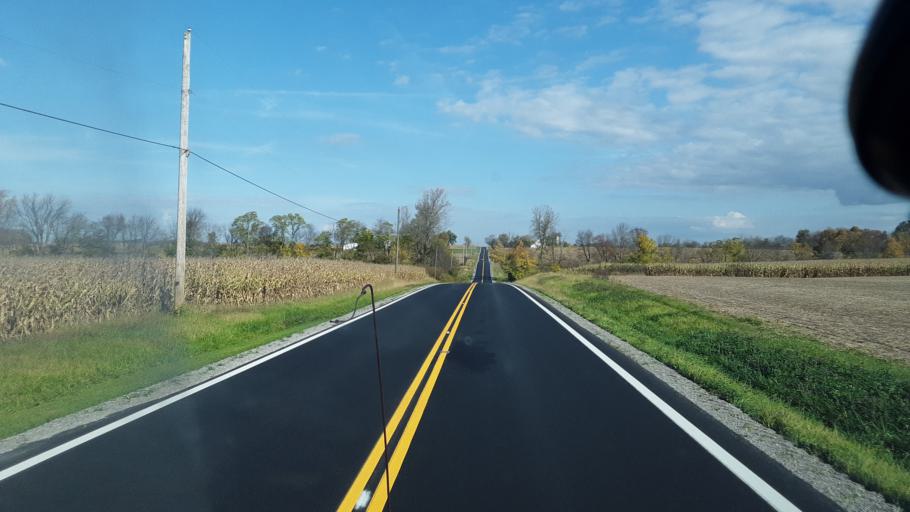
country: US
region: Ohio
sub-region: Highland County
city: Leesburg
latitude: 39.3024
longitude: -83.5891
